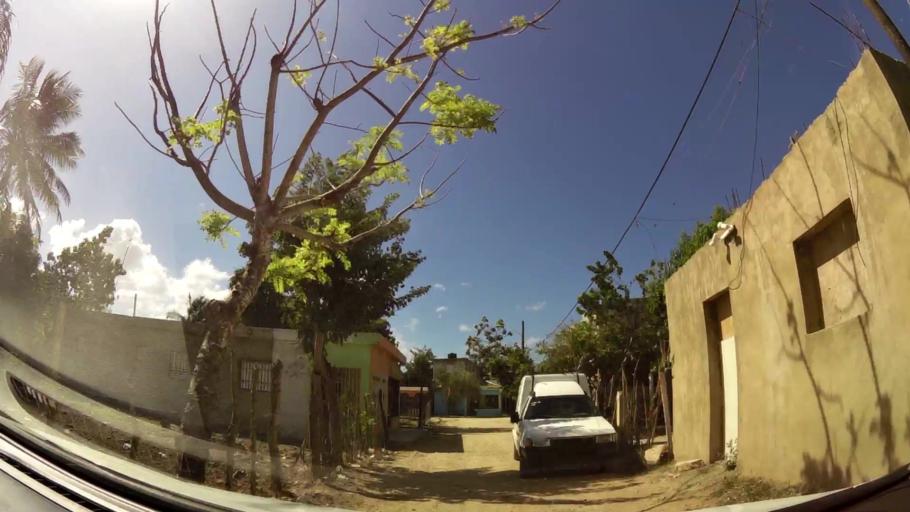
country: DO
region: Santo Domingo
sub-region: Santo Domingo
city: Boca Chica
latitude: 18.4581
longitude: -69.6267
